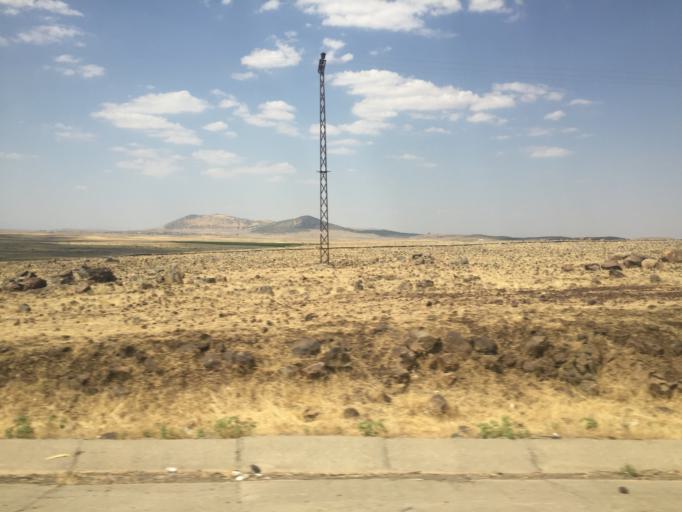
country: TR
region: Sanliurfa
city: Karacadag
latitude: 37.8513
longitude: 39.7196
